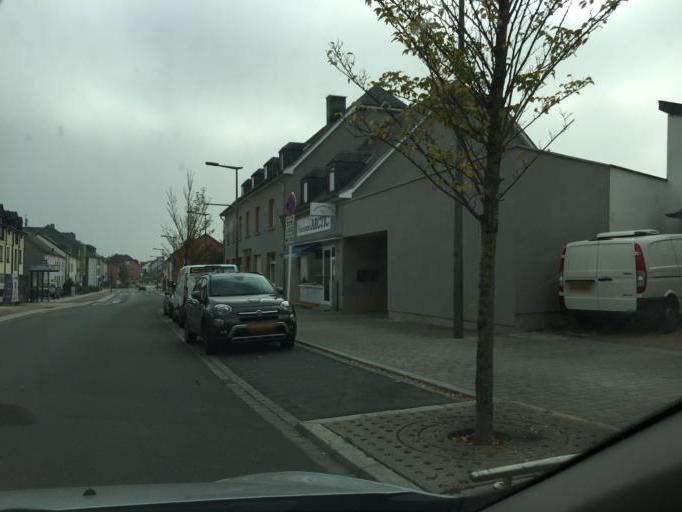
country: LU
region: Luxembourg
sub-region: Canton de Luxembourg
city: Sandweiler
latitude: 49.6160
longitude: 6.2206
